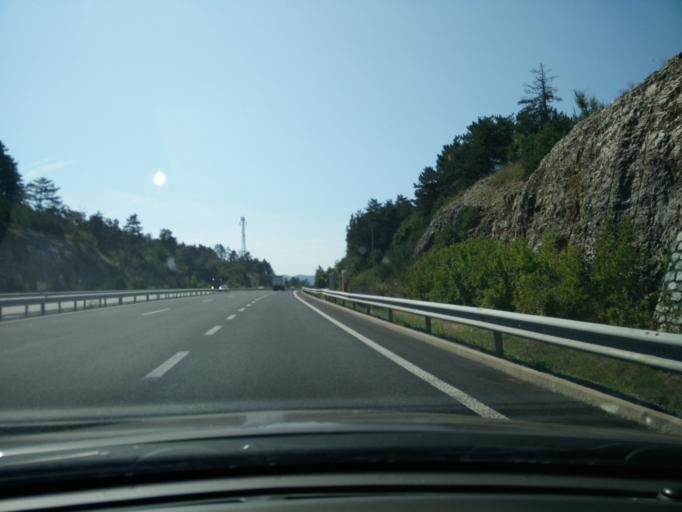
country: SI
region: Hrpelje-Kozina
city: Kozina
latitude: 45.6379
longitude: 13.9616
